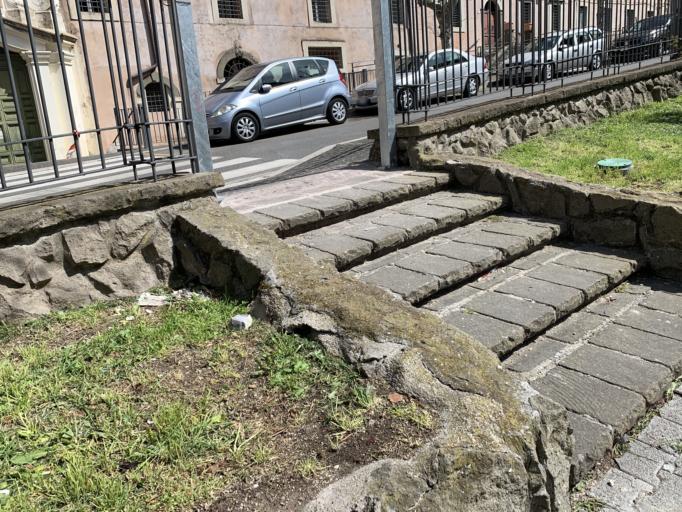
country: IT
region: Latium
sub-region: Citta metropolitana di Roma Capitale
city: Castel Gandolfo
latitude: 41.7711
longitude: 12.6549
